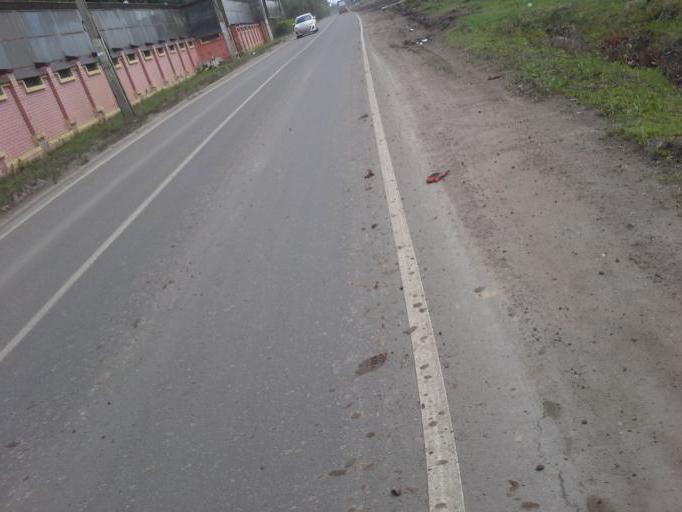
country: RU
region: Moskovskaya
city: Moskovskiy
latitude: 55.5767
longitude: 37.3735
